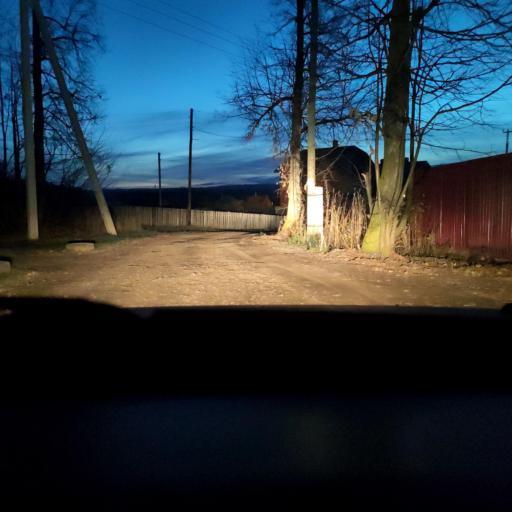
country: RU
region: Perm
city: Ferma
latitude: 57.8957
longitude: 56.3335
